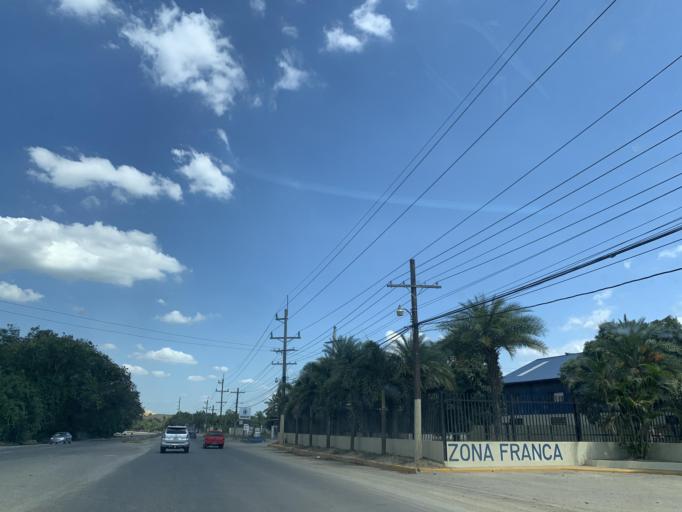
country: DO
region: Santiago
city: Villa Bisono
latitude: 19.5504
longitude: -70.8556
